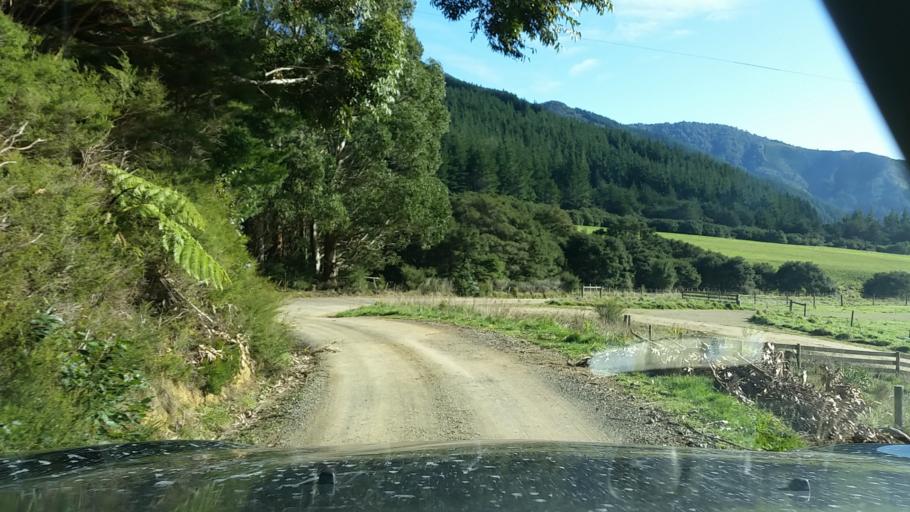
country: NZ
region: Marlborough
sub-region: Marlborough District
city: Picton
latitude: -41.1544
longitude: 173.9684
